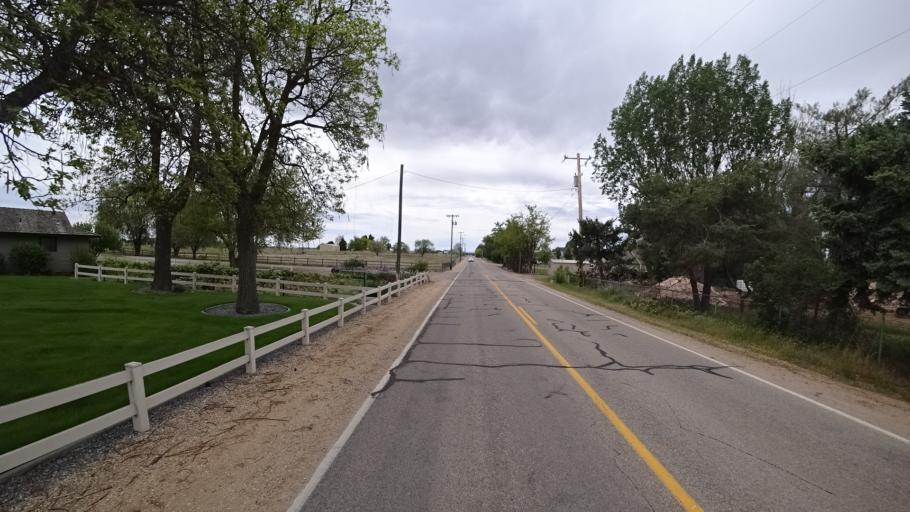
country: US
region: Idaho
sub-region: Ada County
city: Meridian
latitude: 43.5542
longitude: -116.4138
